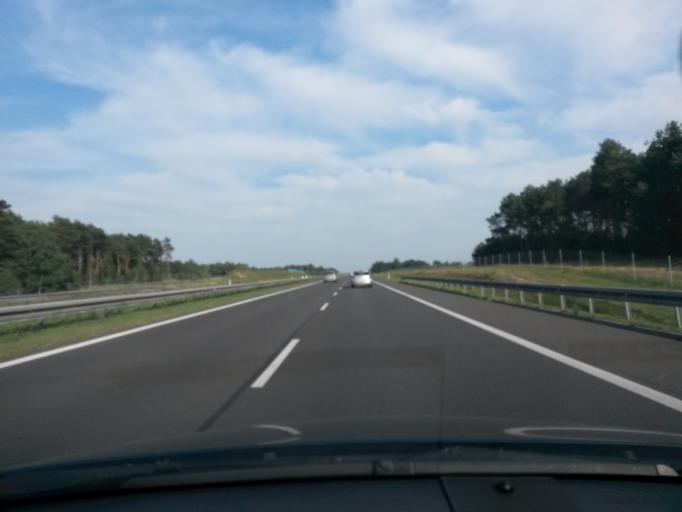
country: PL
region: Greater Poland Voivodeship
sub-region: Powiat slupecki
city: Slupca
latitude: 52.2470
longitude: 17.8525
